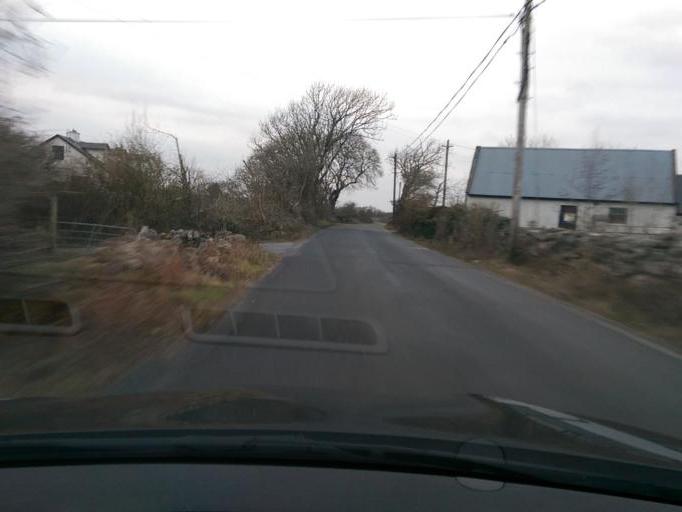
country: IE
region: Connaught
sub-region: County Galway
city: Bearna
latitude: 53.2647
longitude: -9.1541
